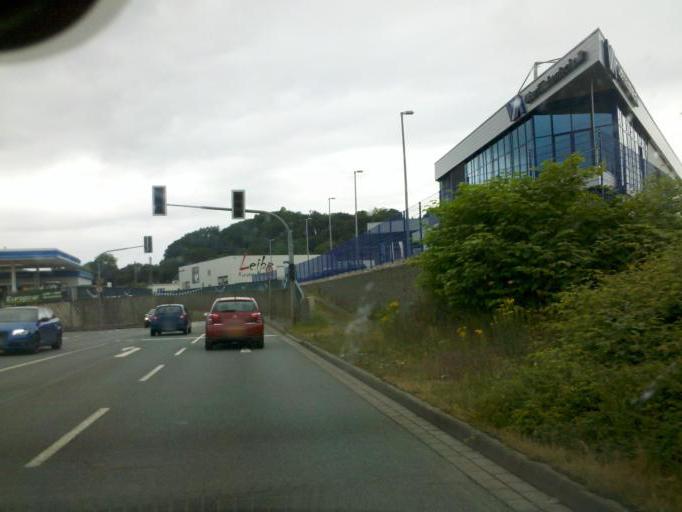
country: DE
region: North Rhine-Westphalia
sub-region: Regierungsbezirk Arnsberg
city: Lennestadt
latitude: 51.1434
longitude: 8.0185
